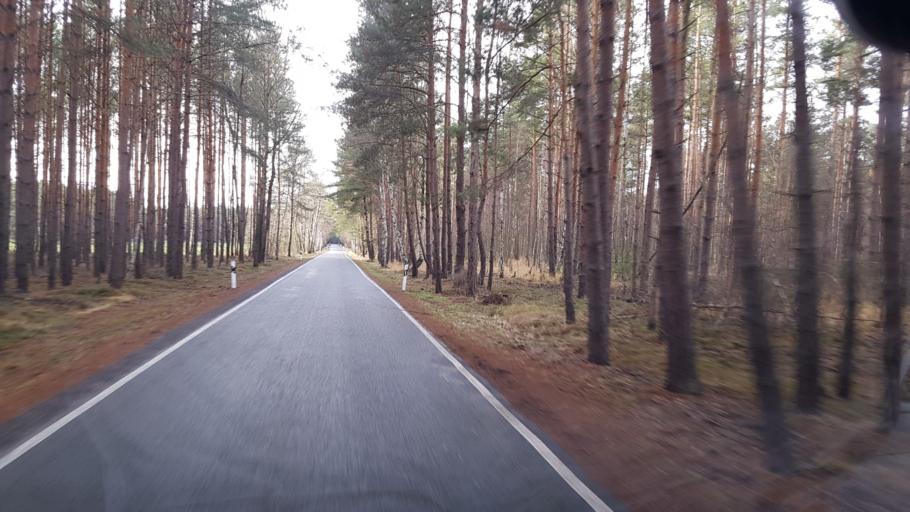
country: DE
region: Brandenburg
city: Bronkow
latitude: 51.6668
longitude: 13.9514
